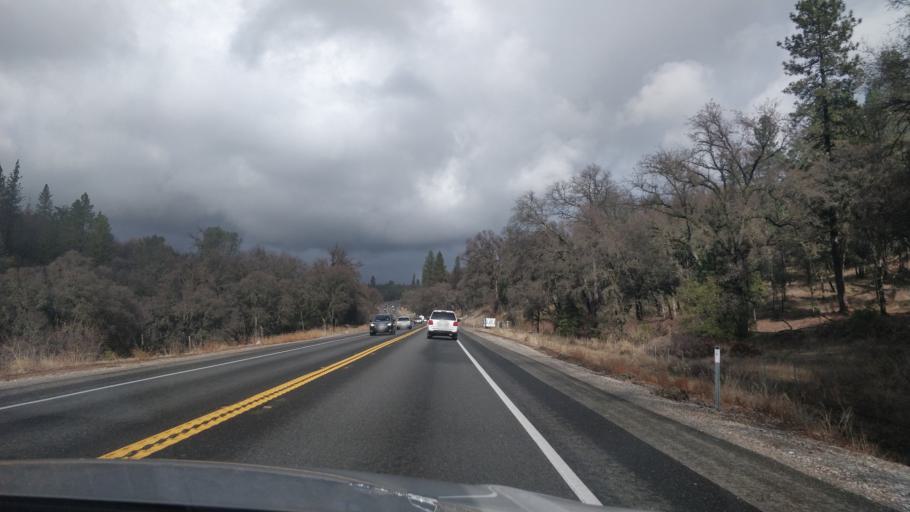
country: US
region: California
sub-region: Nevada County
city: Alta Sierra
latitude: 39.1196
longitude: -121.0795
